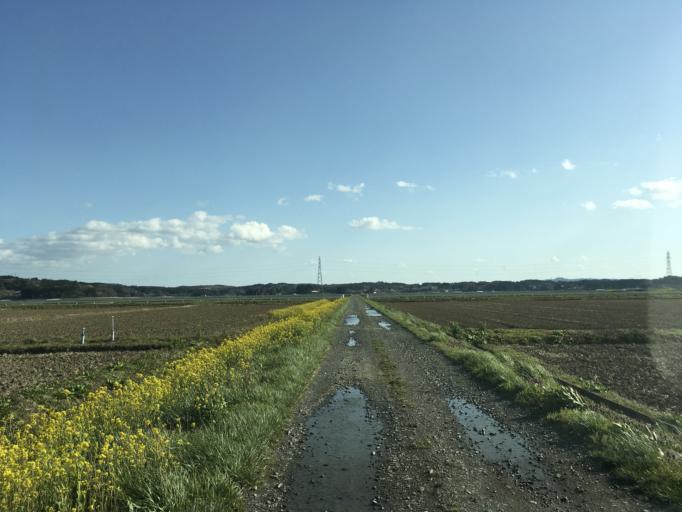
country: JP
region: Miyagi
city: Wakuya
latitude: 38.6599
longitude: 141.2413
